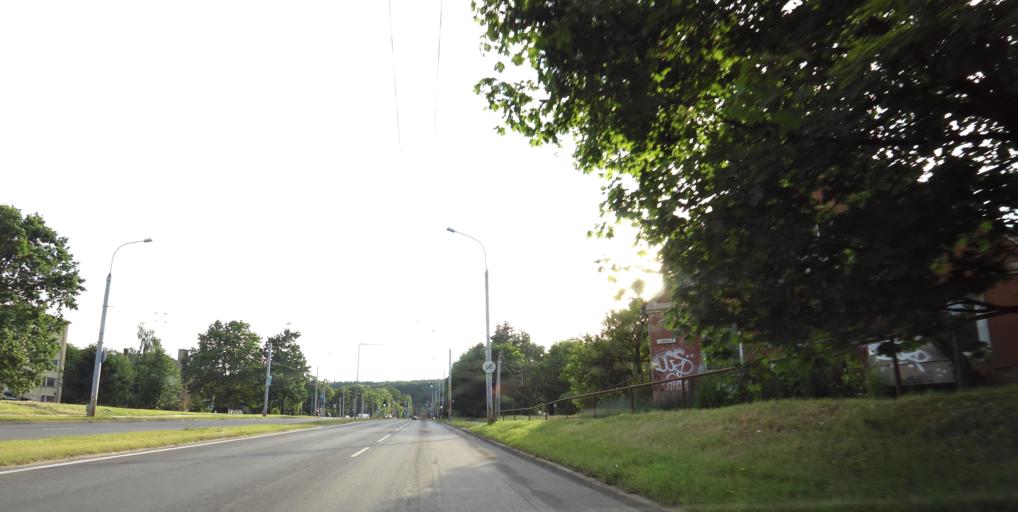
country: LT
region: Vilnius County
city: Seskine
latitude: 54.6997
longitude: 25.2471
